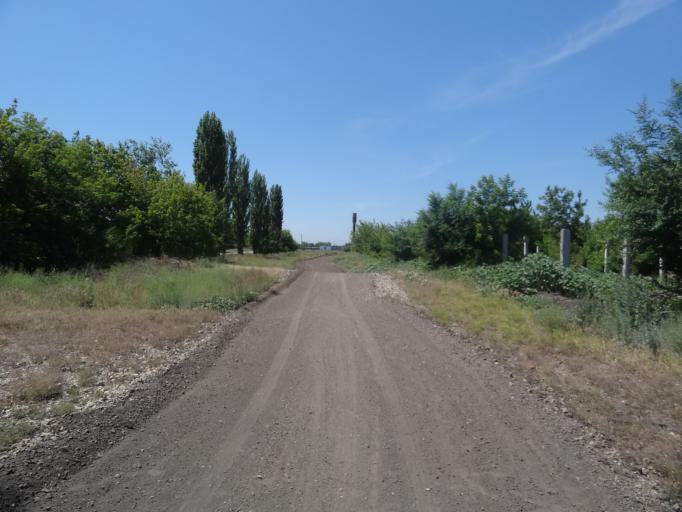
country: RU
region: Saratov
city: Krasnoarmeysk
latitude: 51.1224
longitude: 45.9534
